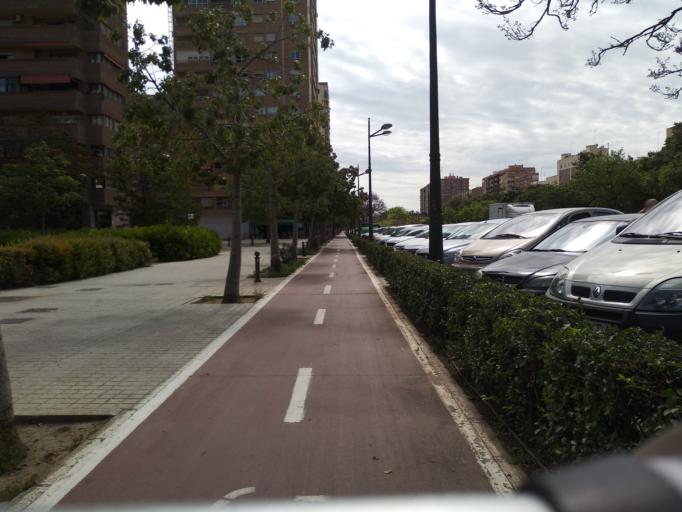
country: ES
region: Valencia
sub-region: Provincia de Valencia
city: Alboraya
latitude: 39.4724
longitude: -0.3414
